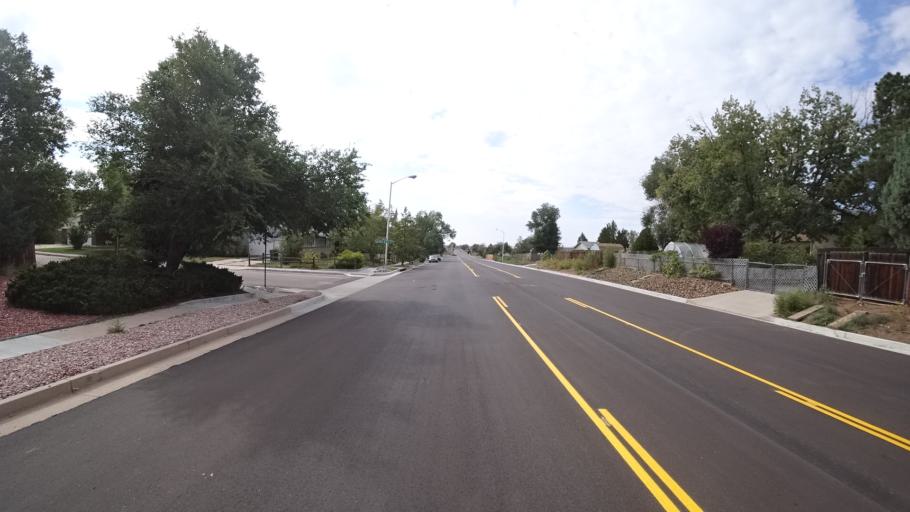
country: US
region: Colorado
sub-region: El Paso County
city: Cimarron Hills
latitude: 38.8491
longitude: -104.7294
